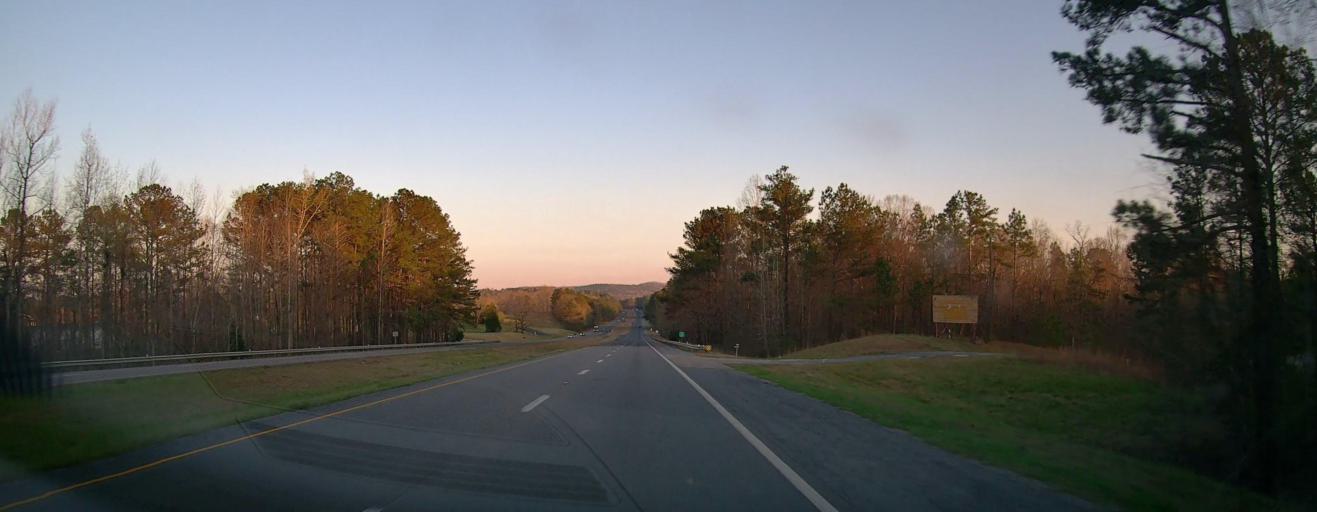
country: US
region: Alabama
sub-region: Coosa County
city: Stewartville
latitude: 33.1049
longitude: -86.2275
